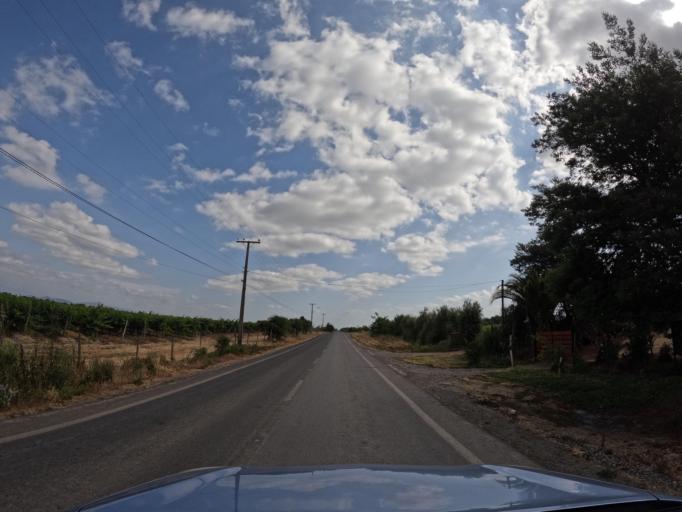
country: CL
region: Maule
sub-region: Provincia de Curico
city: Molina
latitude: -35.1743
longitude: -71.2928
